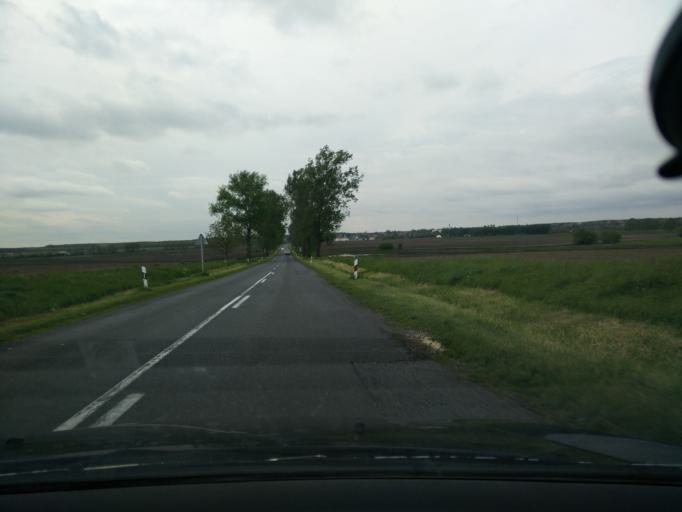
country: HU
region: Gyor-Moson-Sopron
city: Tet
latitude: 47.4451
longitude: 17.4826
